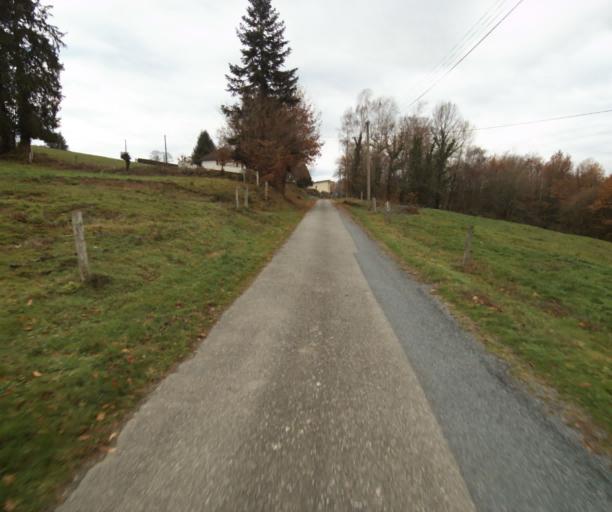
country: FR
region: Limousin
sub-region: Departement de la Correze
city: Sainte-Fortunade
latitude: 45.2277
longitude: 1.7579
